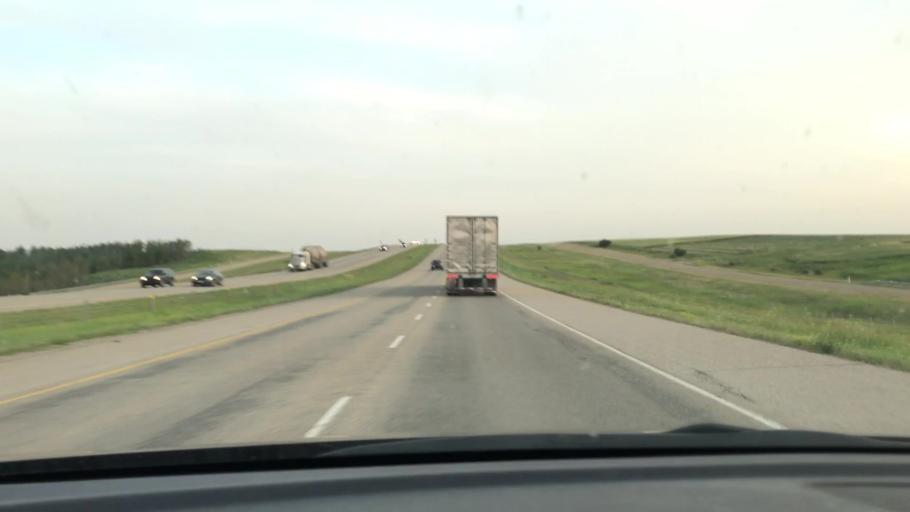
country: CA
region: Alberta
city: Carstairs
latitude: 51.5784
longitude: -114.0252
